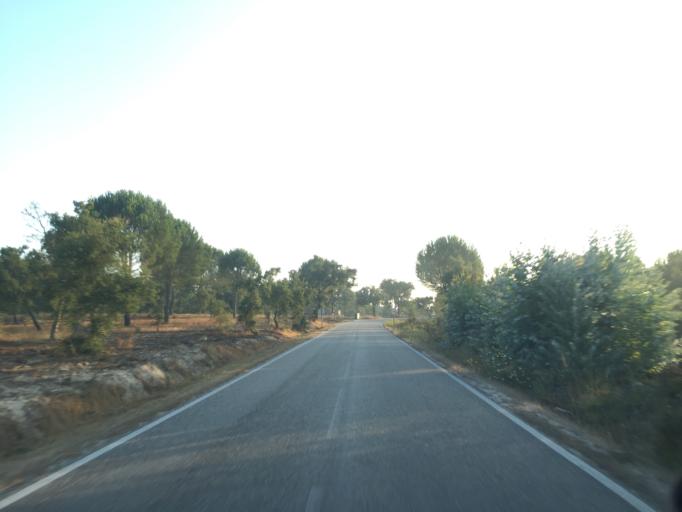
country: PT
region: Santarem
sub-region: Coruche
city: Coruche
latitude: 39.0470
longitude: -8.4326
